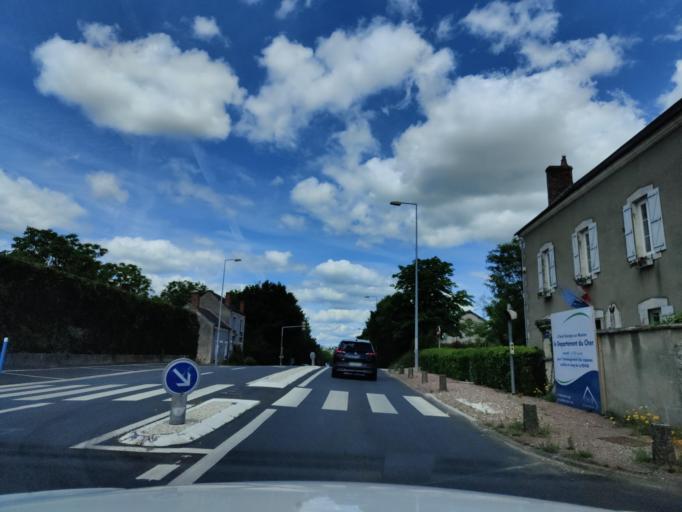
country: FR
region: Centre
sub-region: Departement du Cher
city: Fussy
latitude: 47.1904
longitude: 2.4234
